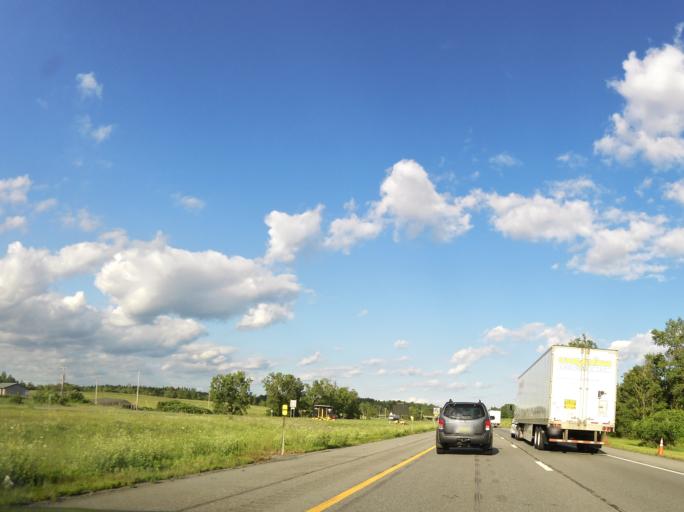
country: US
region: New York
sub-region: Genesee County
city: Oakfield
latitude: 43.0165
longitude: -78.2582
